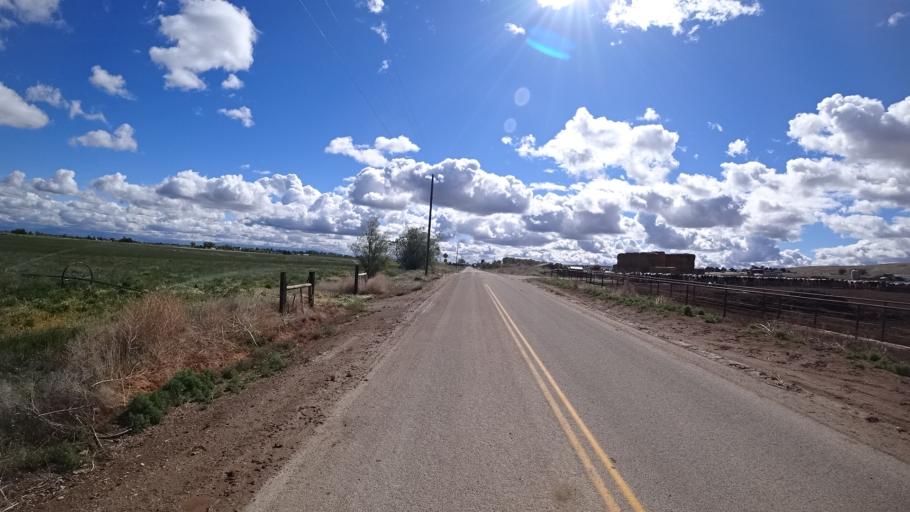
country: US
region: Idaho
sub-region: Ada County
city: Kuna
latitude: 43.4666
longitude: -116.4627
